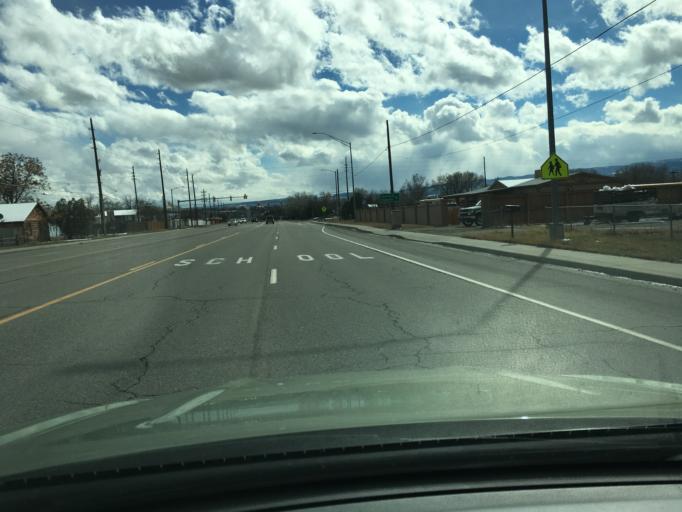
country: US
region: Colorado
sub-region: Mesa County
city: Clifton
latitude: 39.0715
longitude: -108.4595
